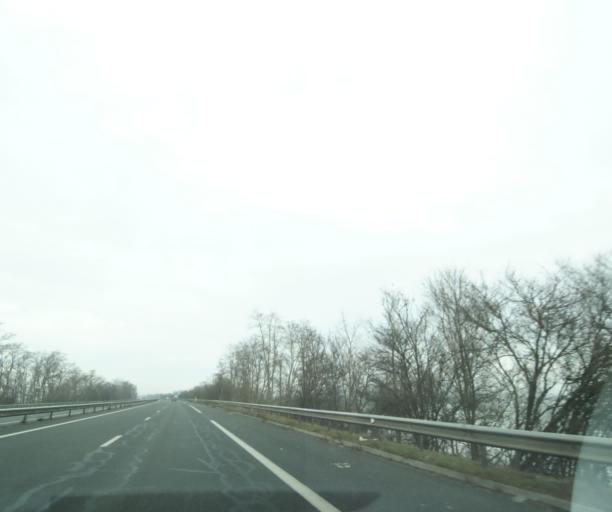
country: FR
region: Auvergne
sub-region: Departement du Puy-de-Dome
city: Riom
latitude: 45.9137
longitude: 3.1519
